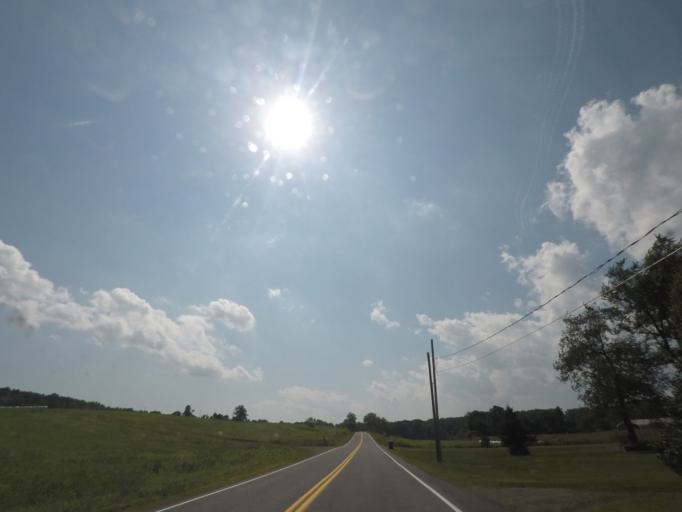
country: US
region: New York
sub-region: Rensselaer County
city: Poestenkill
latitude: 42.8107
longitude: -73.5114
